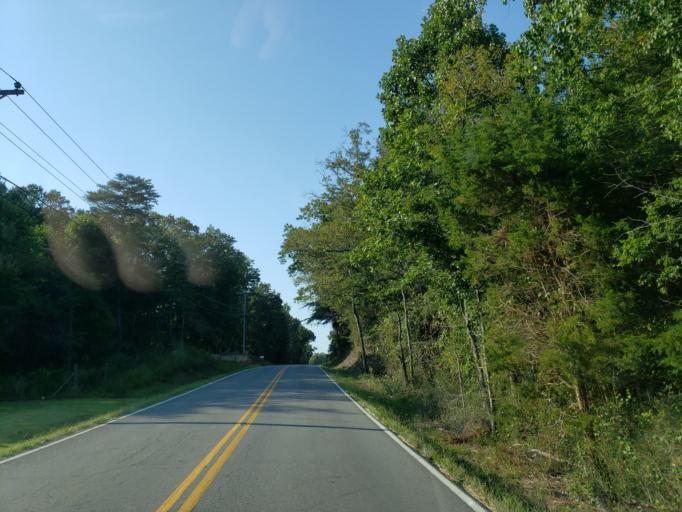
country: US
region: Tennessee
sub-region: Bradley County
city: Wildwood Lake
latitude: 35.0371
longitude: -84.7419
